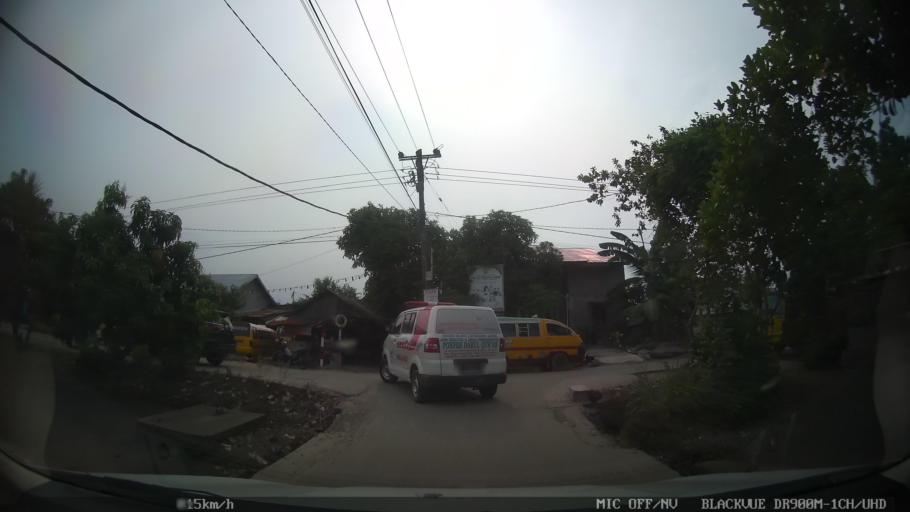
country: ID
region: North Sumatra
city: Medan
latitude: 3.5696
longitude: 98.7478
